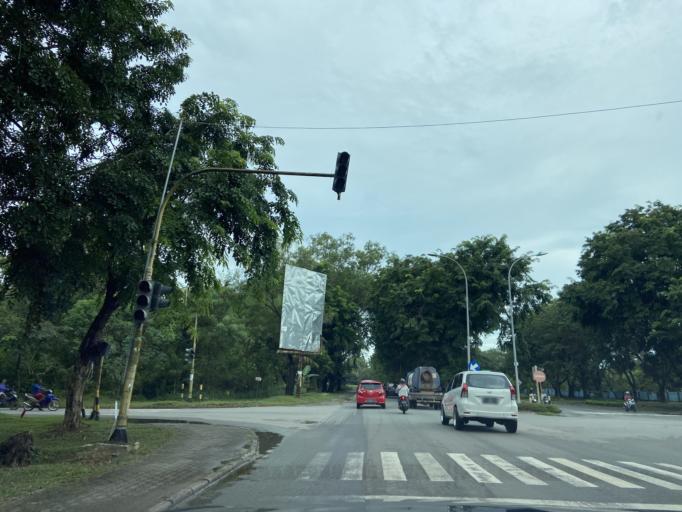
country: SG
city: Singapore
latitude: 1.1125
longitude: 103.9461
